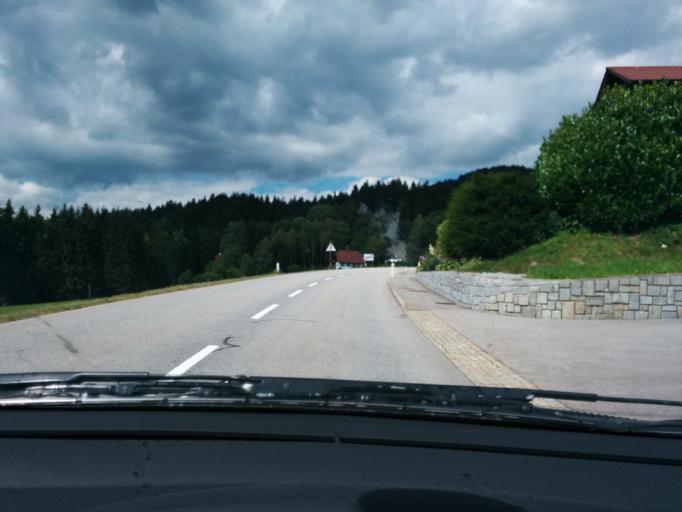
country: AT
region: Upper Austria
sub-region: Politischer Bezirk Rohrbach
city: Ulrichsberg
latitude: 48.7105
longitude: 13.9015
